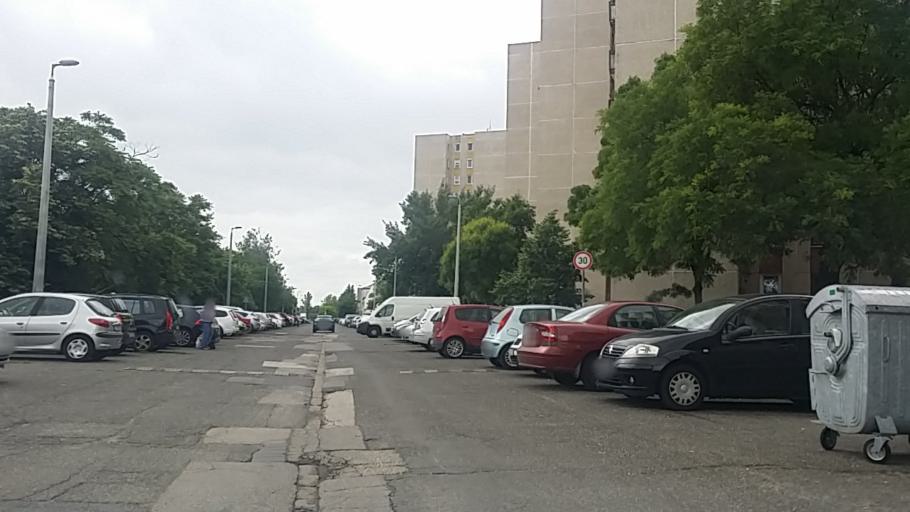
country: HU
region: Budapest
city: Budapest XX. keruelet
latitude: 47.4245
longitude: 19.0889
